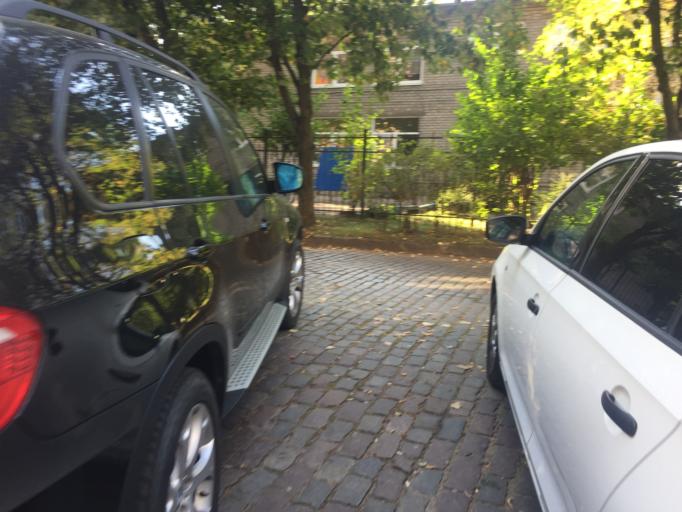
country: RU
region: Kaliningrad
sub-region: Gorod Kaliningrad
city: Kaliningrad
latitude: 54.7019
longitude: 20.5116
